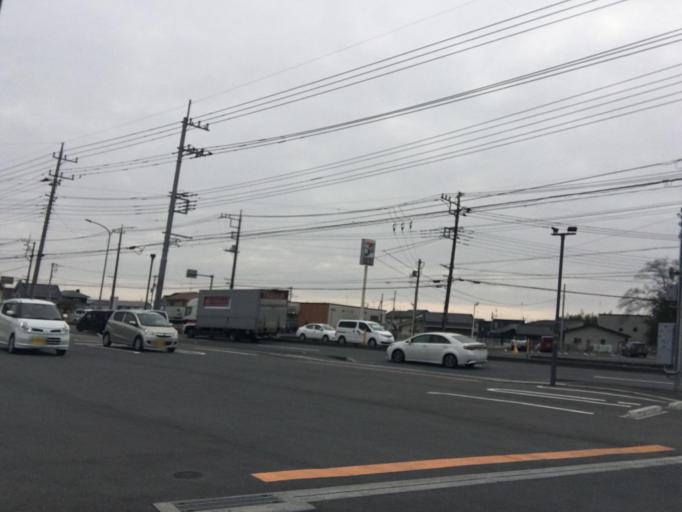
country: JP
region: Saitama
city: Yorii
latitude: 36.1241
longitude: 139.1960
